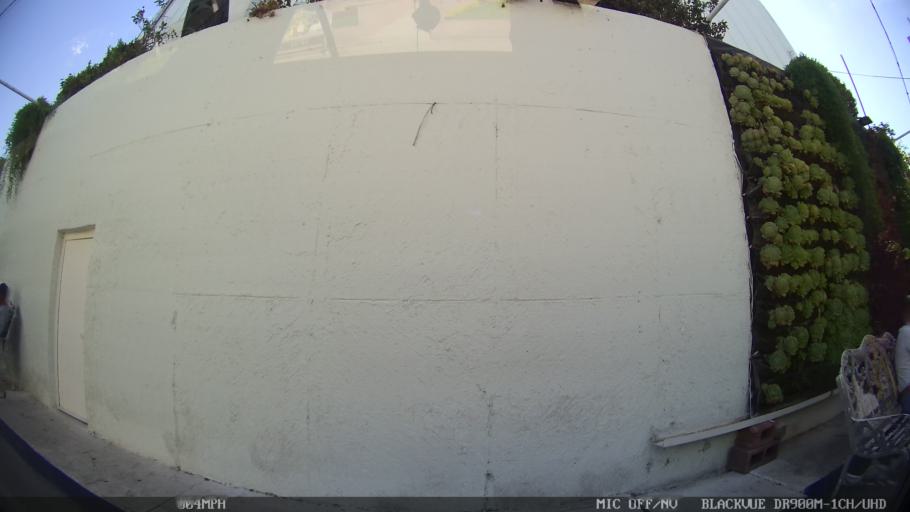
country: MX
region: Jalisco
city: Tlaquepaque
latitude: 20.6718
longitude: -103.2837
